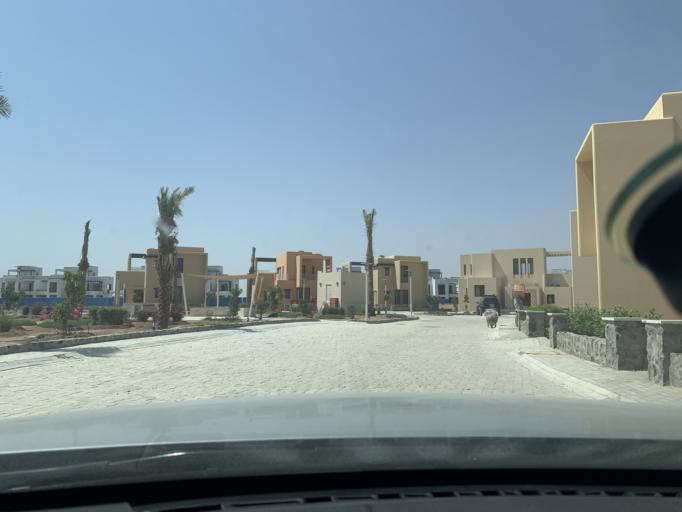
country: EG
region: Red Sea
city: El Gouna
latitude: 27.4022
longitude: 33.6594
